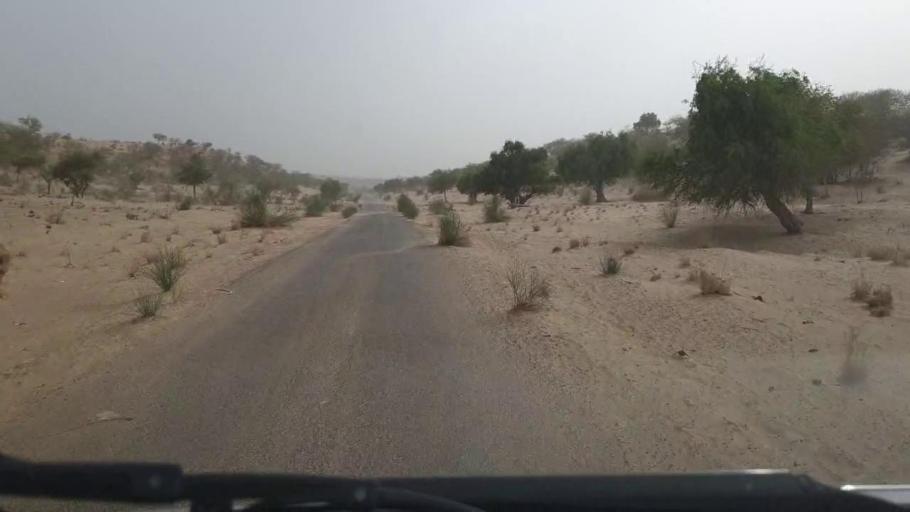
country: PK
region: Sindh
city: Islamkot
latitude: 25.0608
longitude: 70.5354
